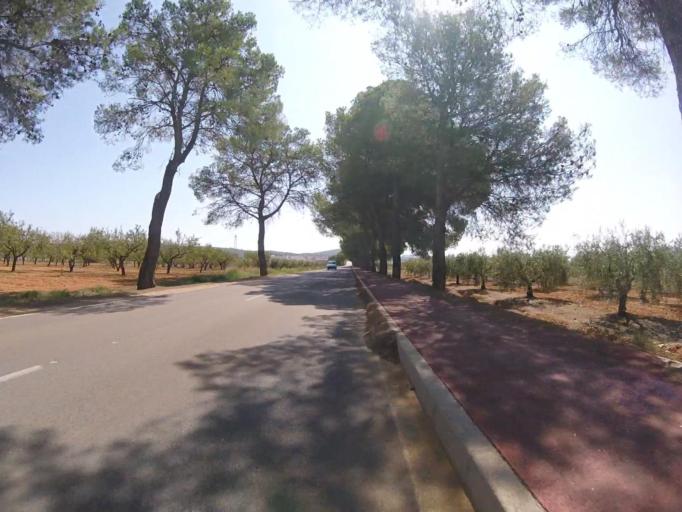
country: ES
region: Valencia
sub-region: Provincia de Castello
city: Cabanes
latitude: 40.1606
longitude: 0.0288
